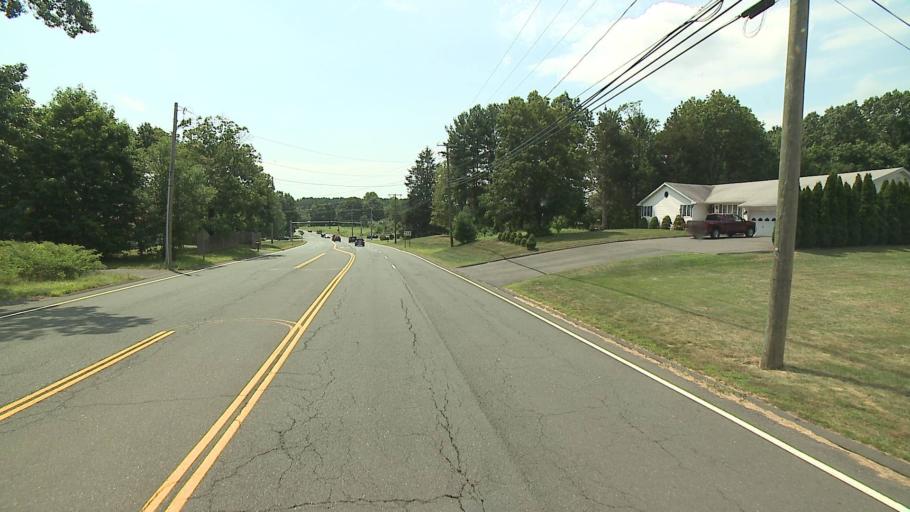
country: US
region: Connecticut
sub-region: Hartford County
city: Plainville
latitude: 41.6935
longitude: -72.8776
